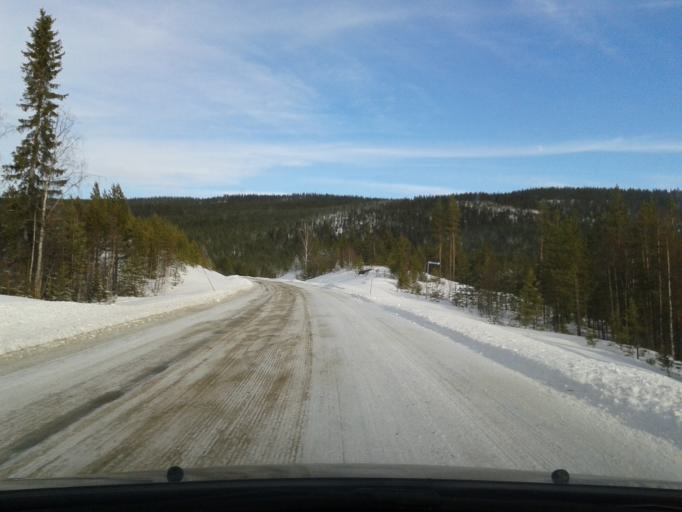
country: SE
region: Vaesterbotten
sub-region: Asele Kommun
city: Asele
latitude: 64.3174
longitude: 17.1956
